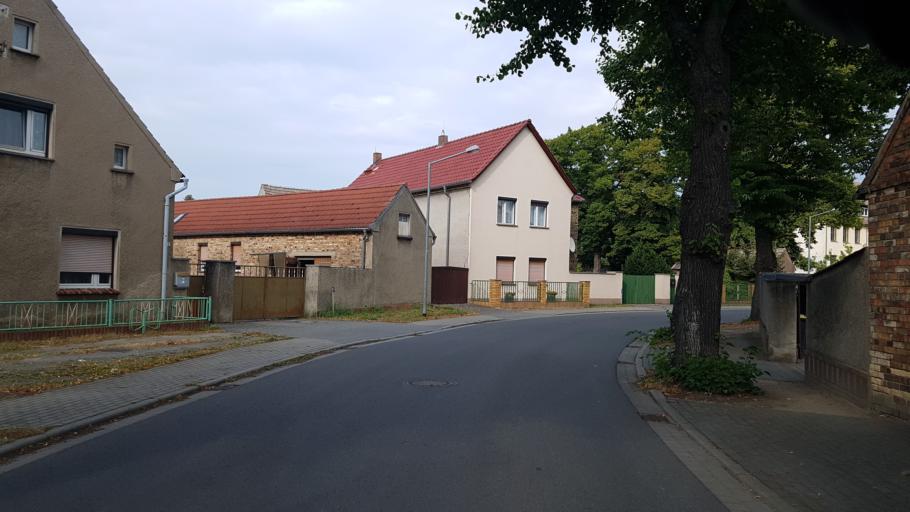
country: DE
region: Brandenburg
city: Lauchhammer
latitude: 51.5134
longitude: 13.6984
